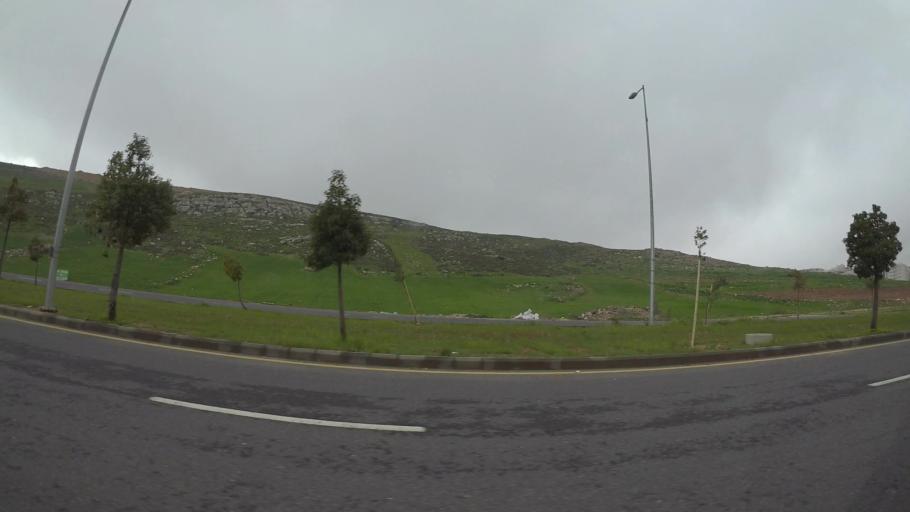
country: JO
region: Amman
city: Al Bunayyat ash Shamaliyah
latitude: 31.9322
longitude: 35.8759
